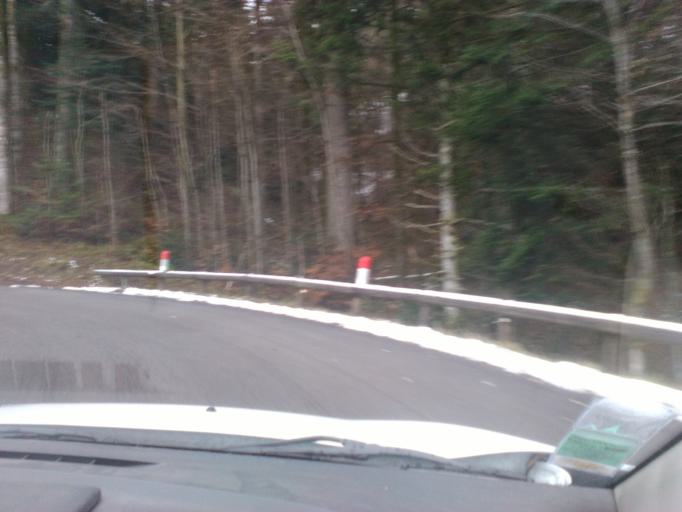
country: FR
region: Lorraine
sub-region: Departement des Vosges
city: Xonrupt-Longemer
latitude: 48.0521
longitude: 6.9790
